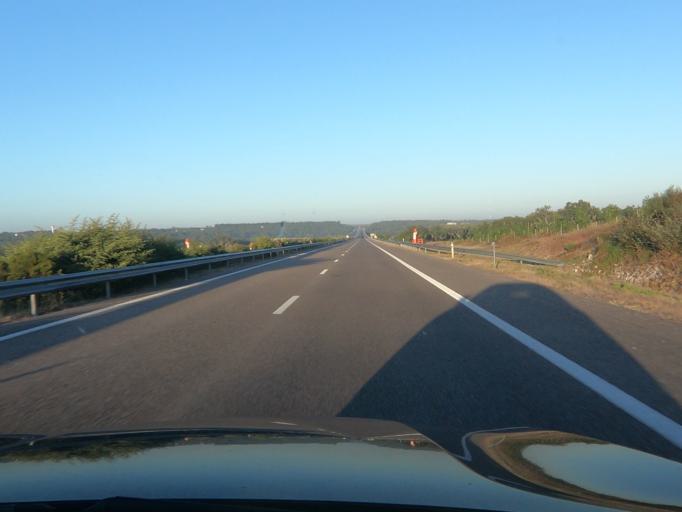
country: PT
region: Santarem
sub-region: Salvaterra de Magos
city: Marinhais
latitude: 39.1104
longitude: -8.6383
